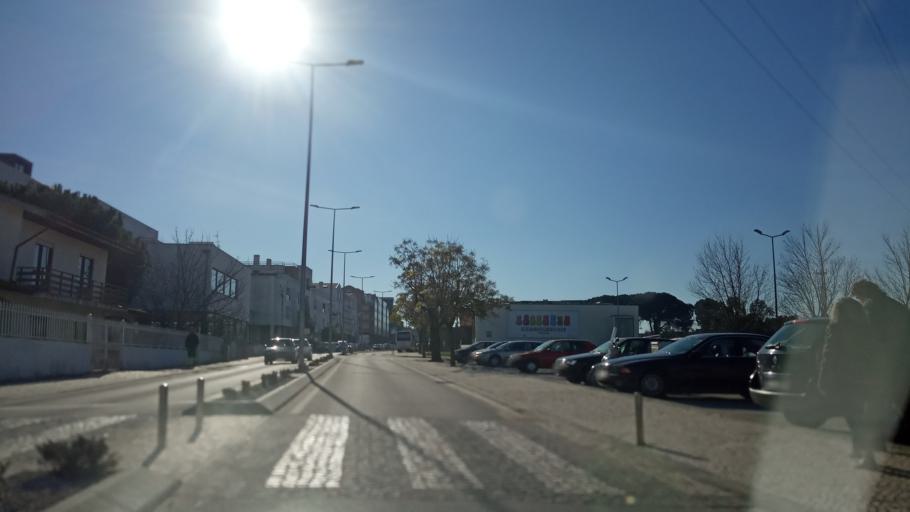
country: PT
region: Aveiro
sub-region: Anadia
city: Anadia
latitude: 40.4391
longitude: -8.4369
